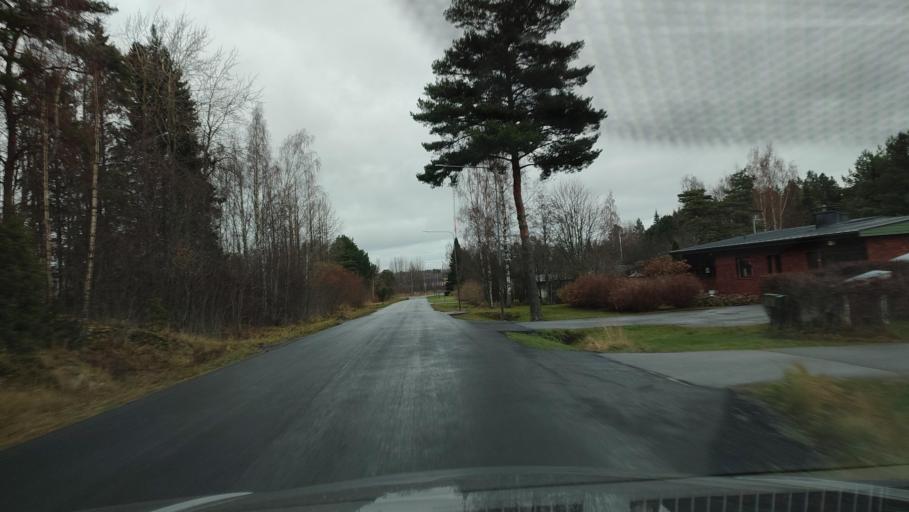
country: FI
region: Ostrobothnia
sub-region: Sydosterbotten
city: Kristinestad
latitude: 62.2743
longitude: 21.3991
